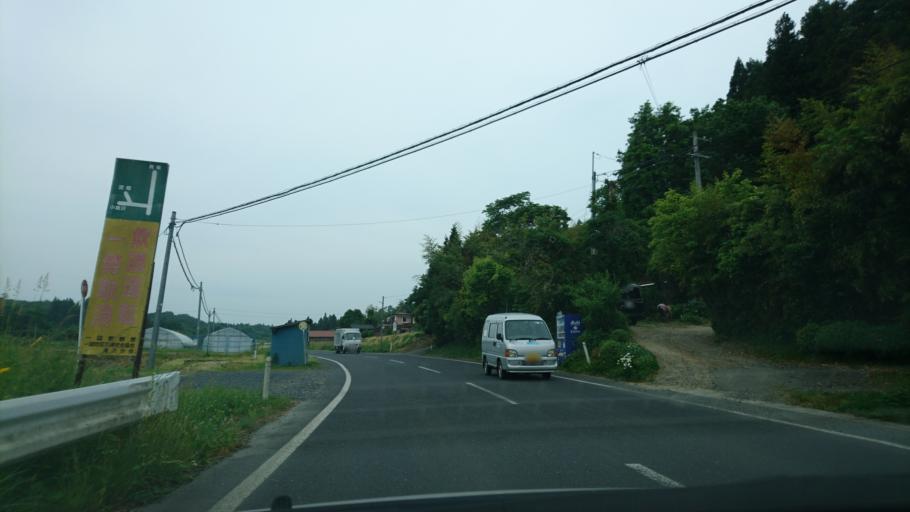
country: JP
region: Iwate
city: Ichinoseki
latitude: 38.9016
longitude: 141.1741
